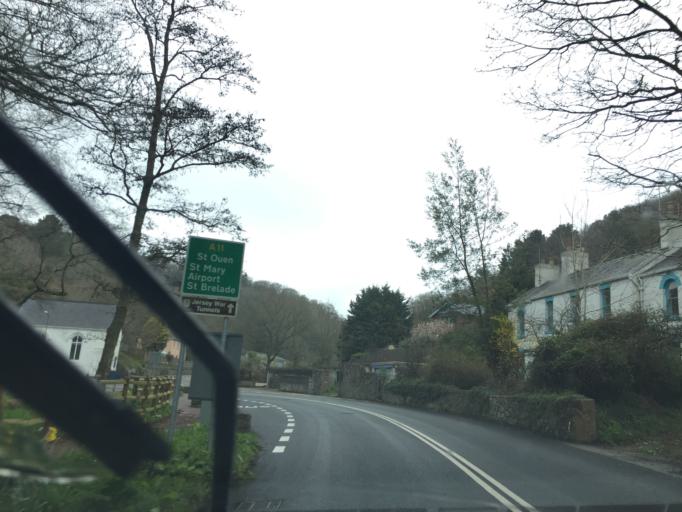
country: JE
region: St Helier
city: Saint Helier
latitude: 49.2043
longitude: -2.1550
